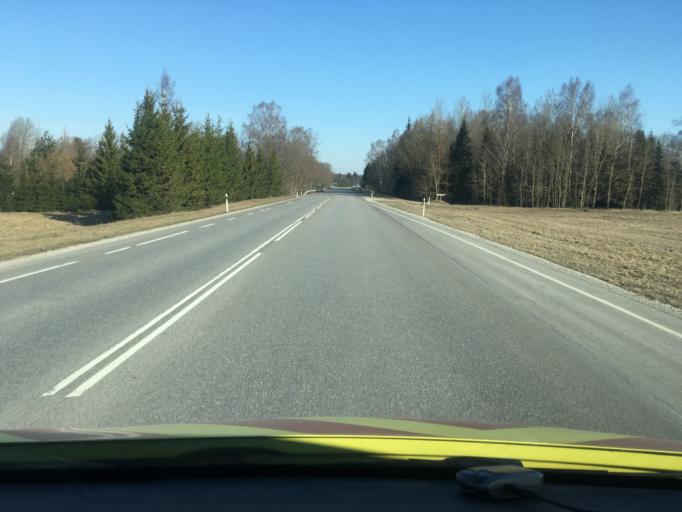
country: EE
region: Harju
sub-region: Saku vald
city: Saku
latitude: 59.2893
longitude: 24.7392
